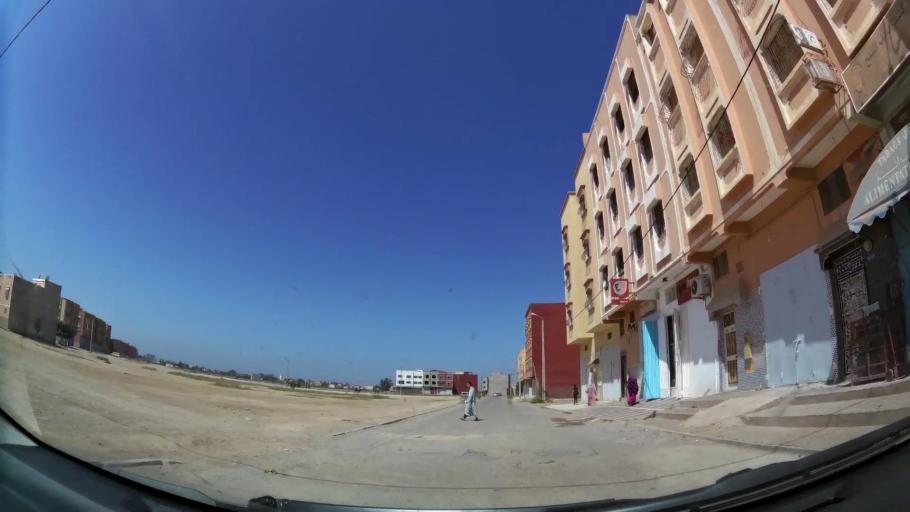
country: MA
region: Souss-Massa-Draa
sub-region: Inezgane-Ait Mellou
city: Inezgane
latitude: 30.3360
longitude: -9.5083
